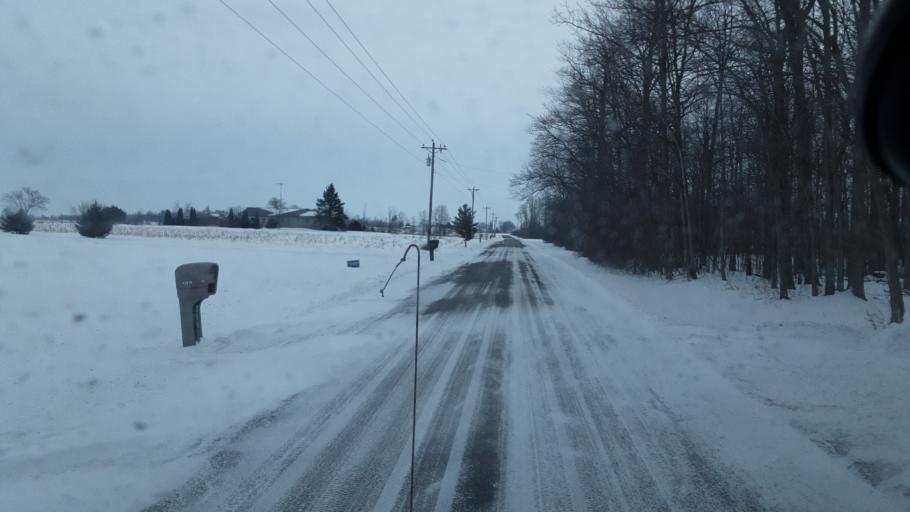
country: US
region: Ohio
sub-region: Union County
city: Marysville
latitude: 40.1748
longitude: -83.3727
